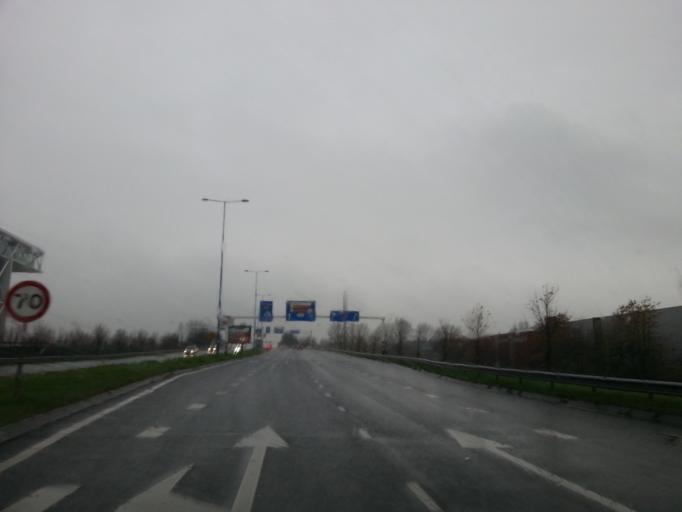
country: NL
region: South Holland
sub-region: Gemeente Zoetermeer
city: Zoetermeer
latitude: 52.0410
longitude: 4.5053
